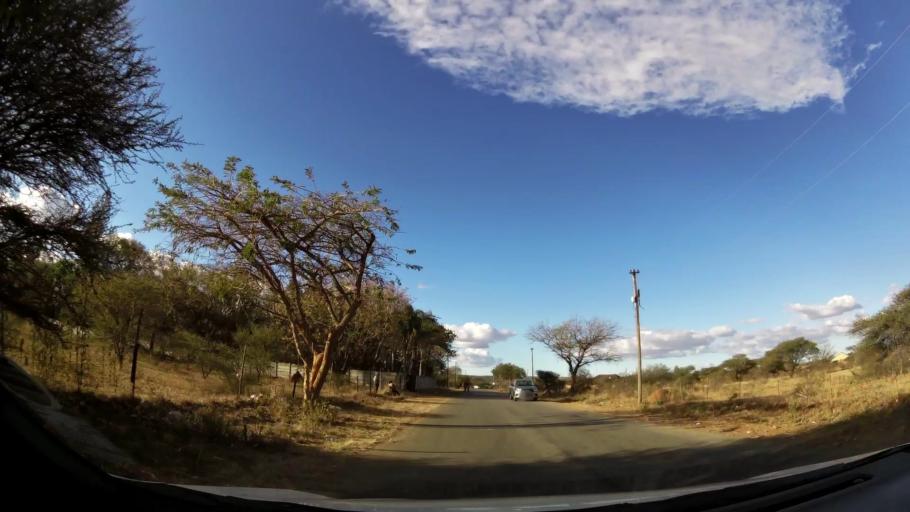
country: ZA
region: Limpopo
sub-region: Capricorn District Municipality
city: Polokwane
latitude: -23.9315
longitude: 29.4390
